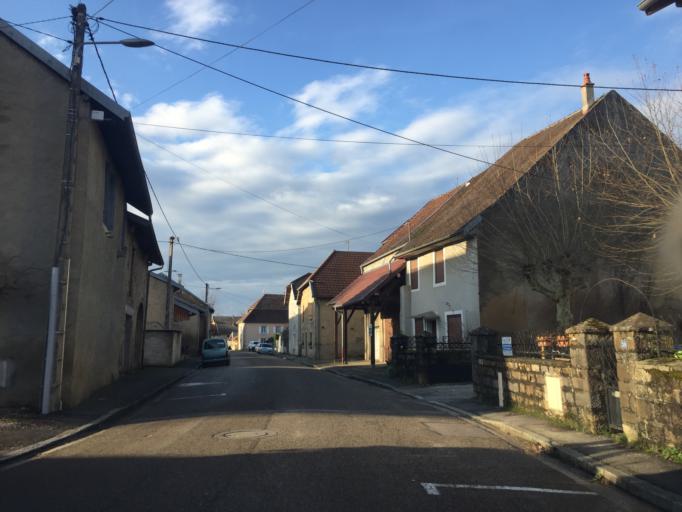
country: FR
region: Franche-Comte
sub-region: Departement du Jura
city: Arbois
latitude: 46.9215
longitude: 5.7539
